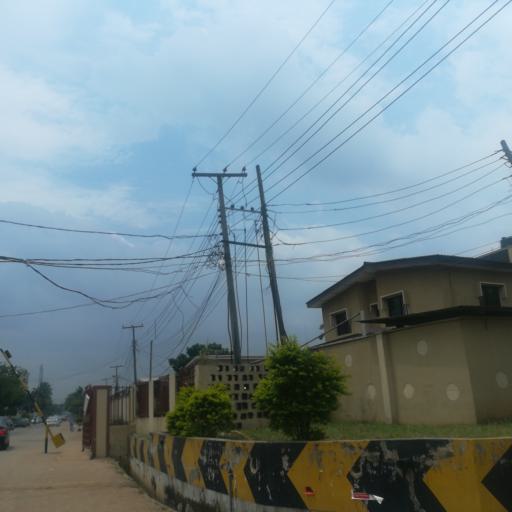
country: NG
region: Lagos
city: Ojota
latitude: 6.5768
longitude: 3.3876
